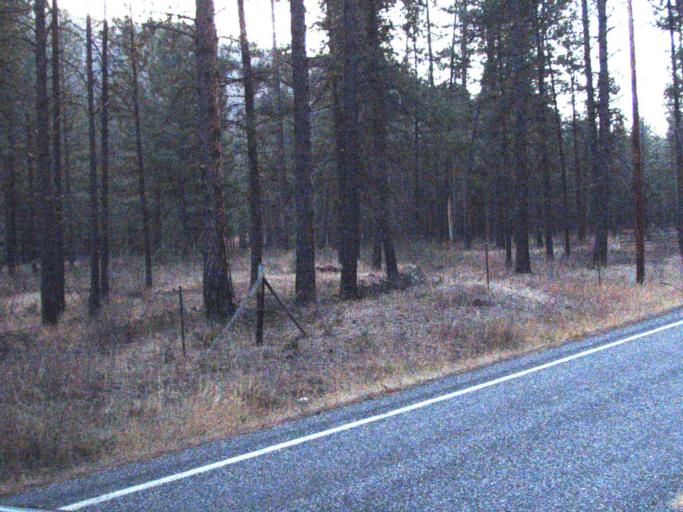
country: US
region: Washington
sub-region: Okanogan County
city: Coulee Dam
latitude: 48.1785
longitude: -118.7089
